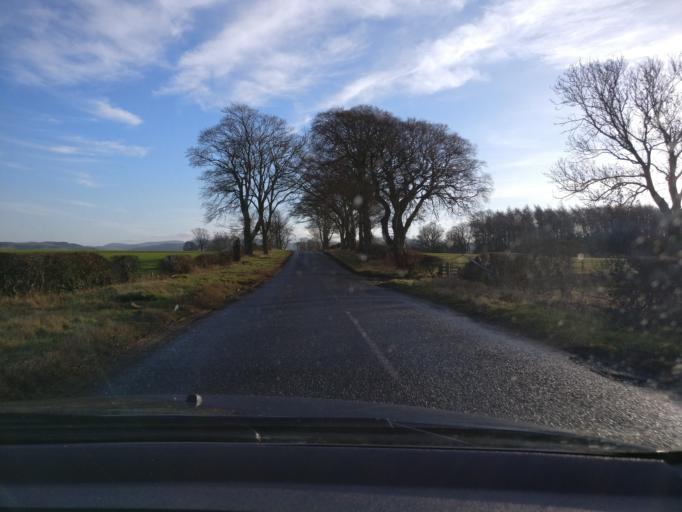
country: GB
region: Scotland
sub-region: The Scottish Borders
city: Kelso
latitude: 55.5279
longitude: -2.4257
